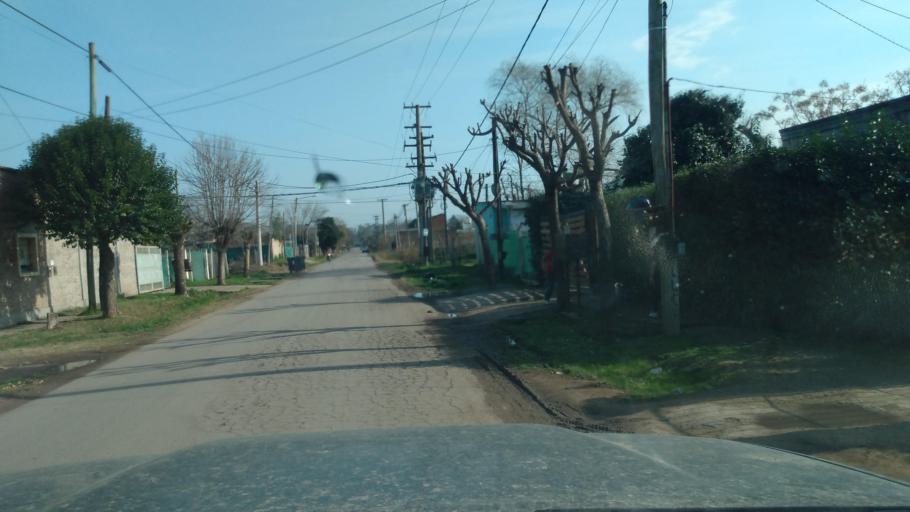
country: AR
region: Buenos Aires
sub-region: Partido de Lujan
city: Lujan
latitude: -34.5721
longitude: -59.0809
